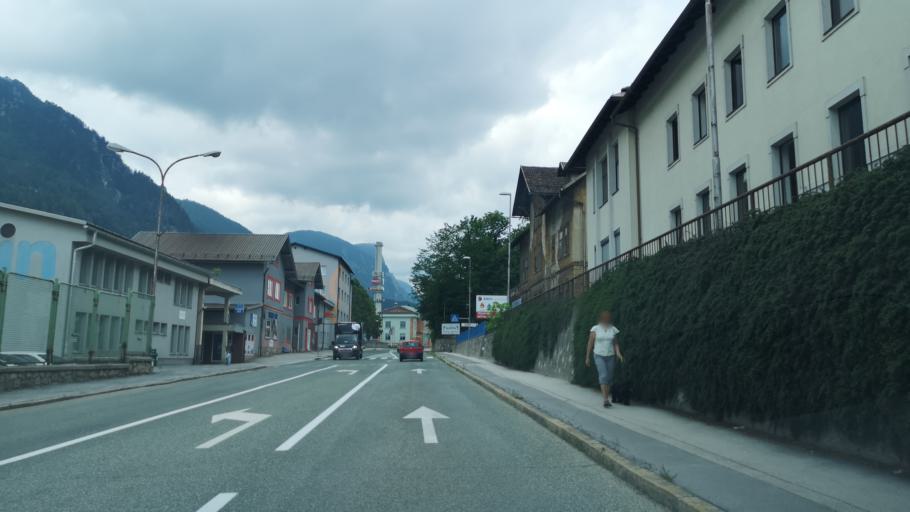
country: SI
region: Jesenice
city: Jesenice
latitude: 46.4315
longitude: 14.0660
